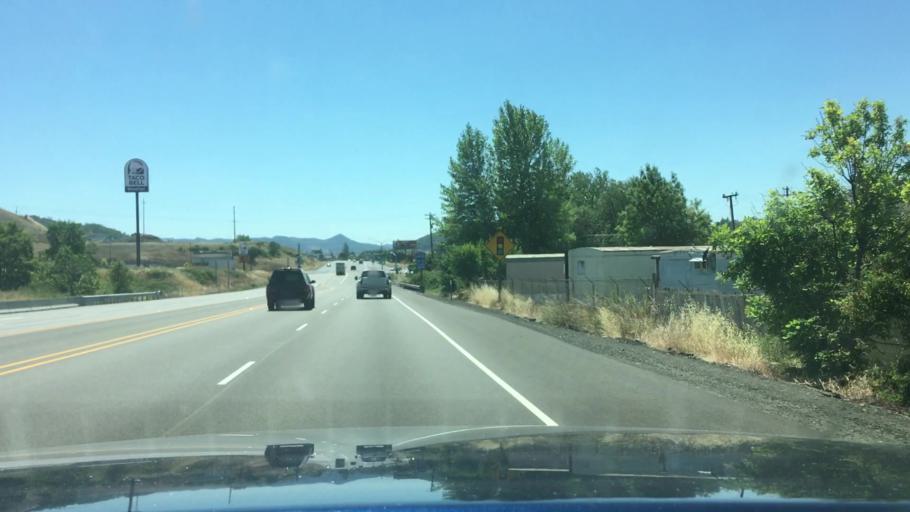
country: US
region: Oregon
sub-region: Douglas County
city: Green
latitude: 43.1512
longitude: -123.3688
